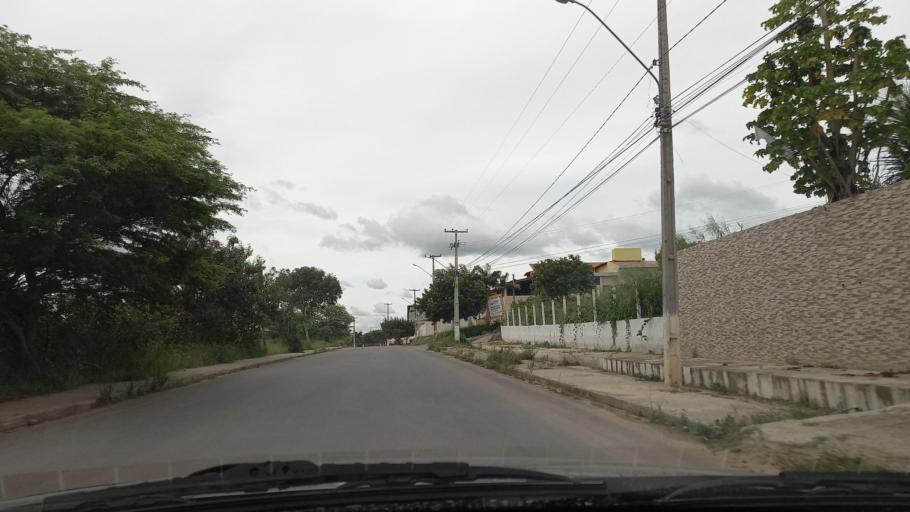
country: BR
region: Pernambuco
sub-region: Gravata
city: Gravata
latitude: -8.2121
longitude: -35.6004
